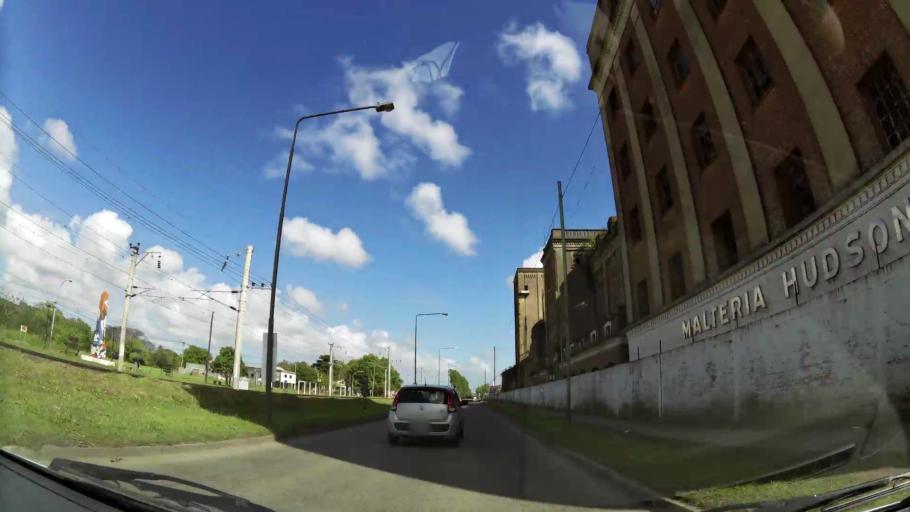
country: AR
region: Buenos Aires
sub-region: Partido de Quilmes
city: Quilmes
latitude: -34.7892
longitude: -58.1584
